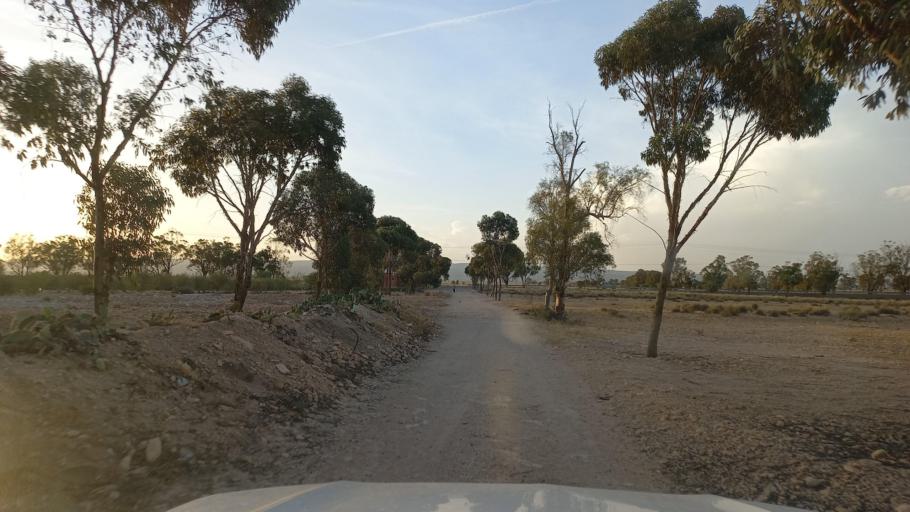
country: TN
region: Al Qasrayn
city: Kasserine
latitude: 35.2415
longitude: 8.9928
